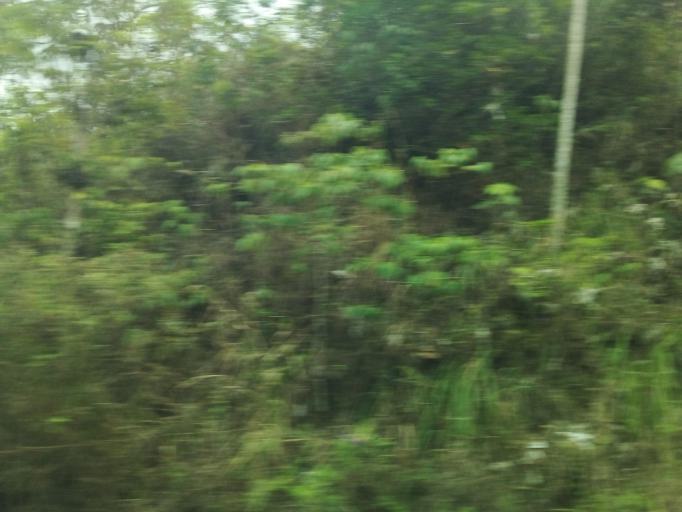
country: BR
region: Minas Gerais
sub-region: Nova Era
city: Nova Era
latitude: -19.6640
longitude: -42.8877
